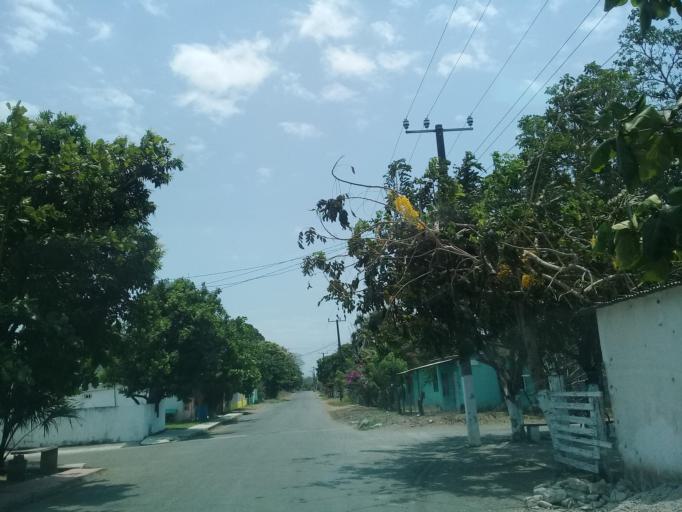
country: MX
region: Veracruz
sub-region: Veracruz
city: Delfino Victoria (Santa Fe)
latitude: 19.1725
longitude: -96.3000
